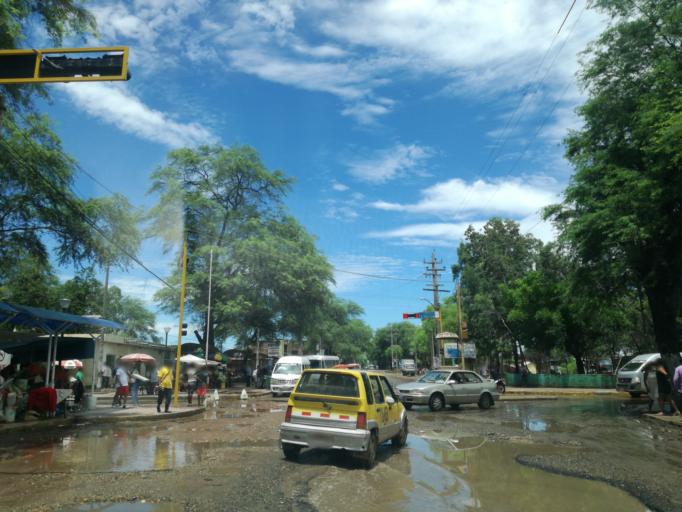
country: PE
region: Piura
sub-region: Provincia de Piura
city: Catacaos
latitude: -5.2657
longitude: -80.6712
